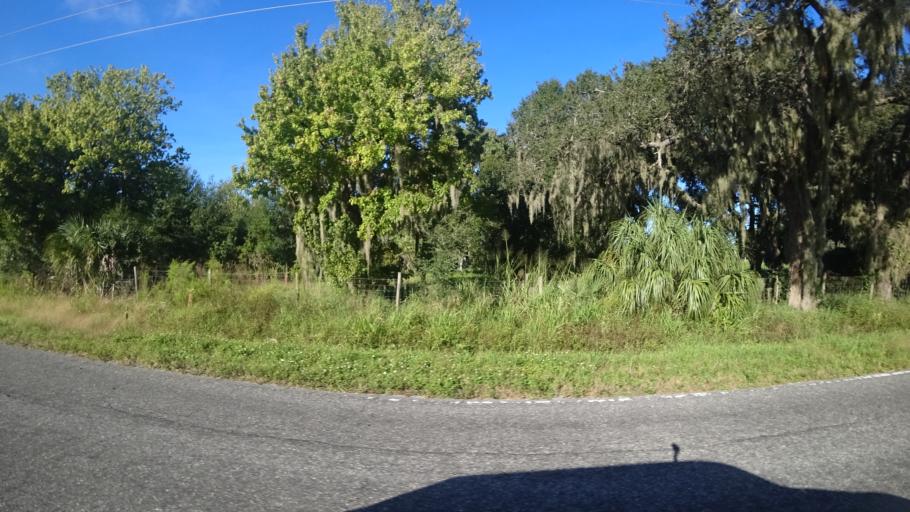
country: US
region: Florida
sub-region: Manatee County
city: Memphis
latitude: 27.5913
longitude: -82.5273
